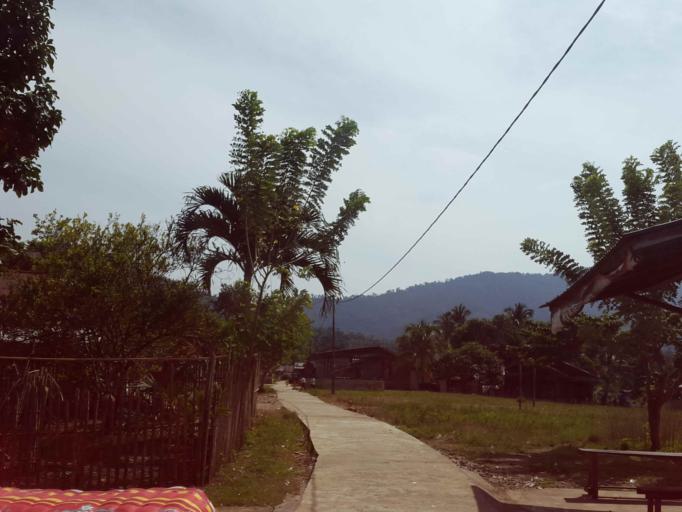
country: MY
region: Sarawak
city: Kuching
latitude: 0.8432
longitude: 110.4851
